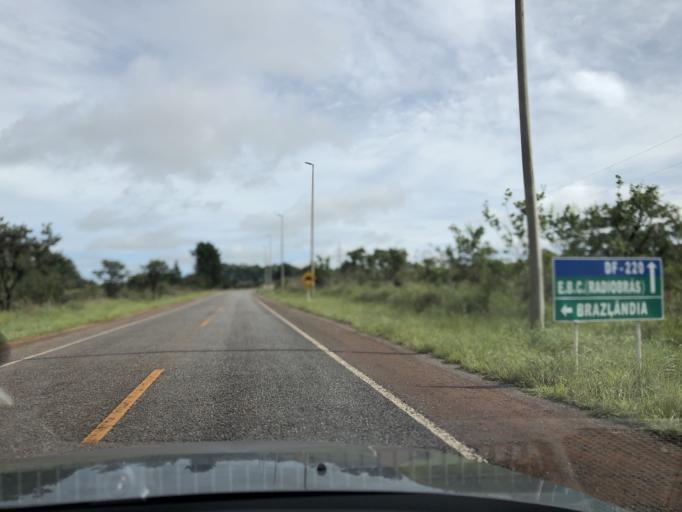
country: BR
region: Federal District
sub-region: Brasilia
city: Brasilia
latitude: -15.6816
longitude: -48.0894
